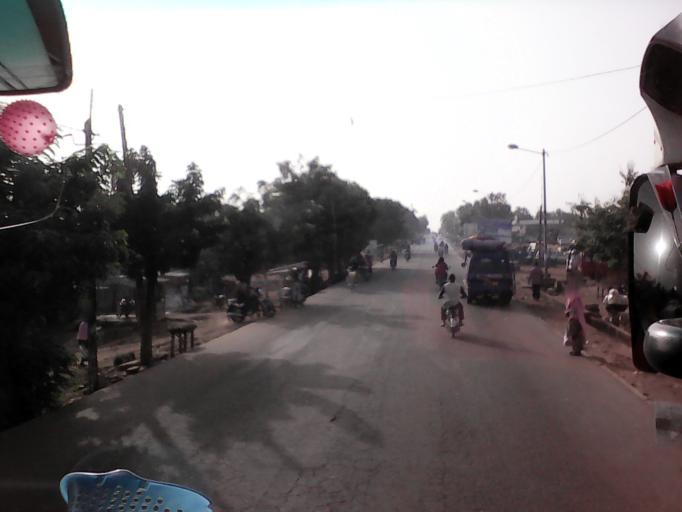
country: TG
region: Kara
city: Kara
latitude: 9.5334
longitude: 1.2003
